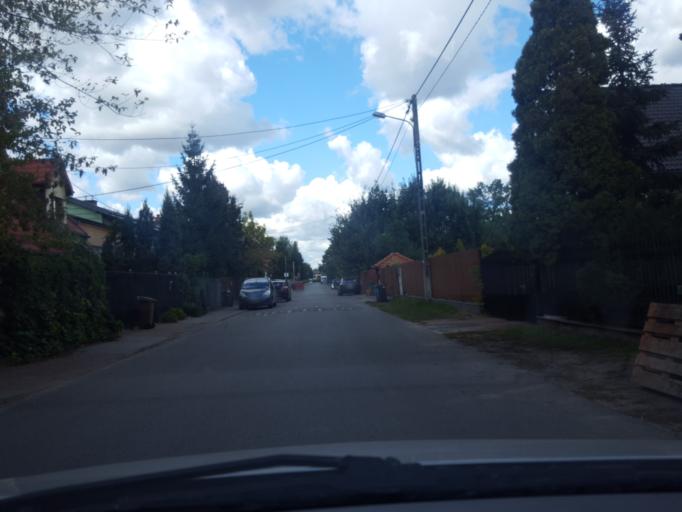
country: PL
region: Masovian Voivodeship
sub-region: Warszawa
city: Rembertow
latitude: 52.2710
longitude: 21.1674
